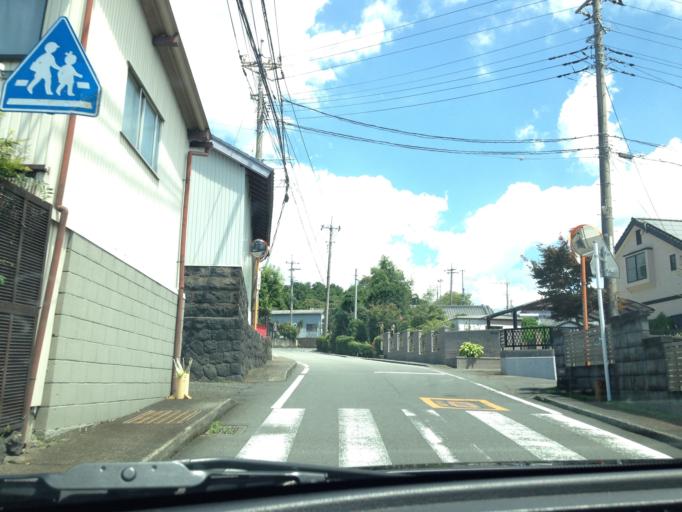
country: JP
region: Shizuoka
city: Fuji
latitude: 35.1948
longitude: 138.7133
